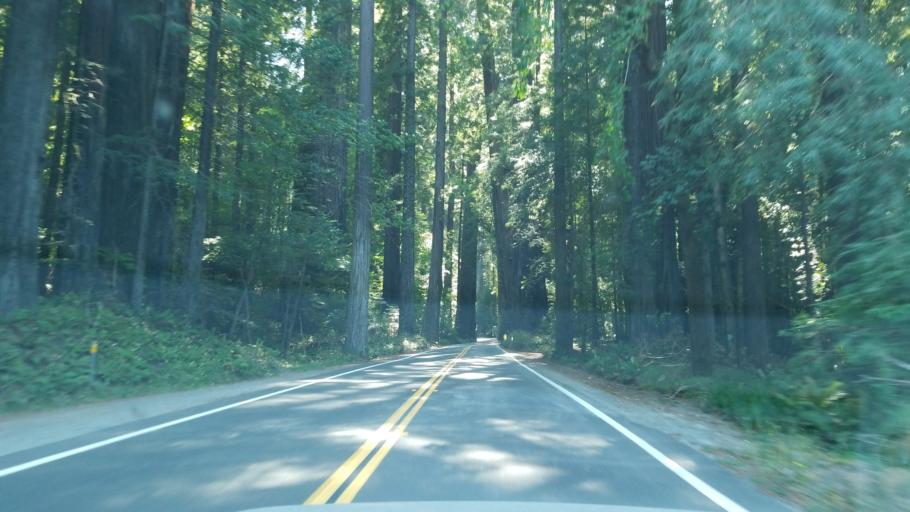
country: US
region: California
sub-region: Humboldt County
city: Redway
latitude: 40.3237
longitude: -123.9268
